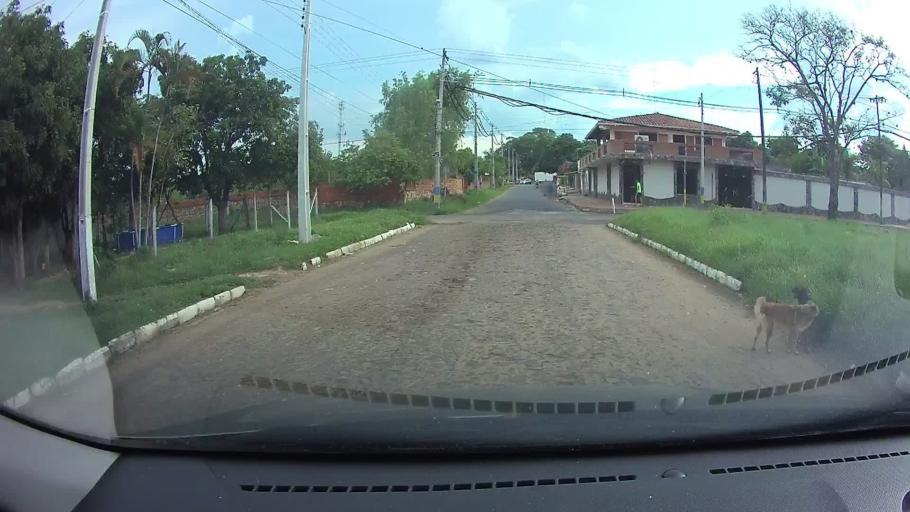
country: PY
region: Central
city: San Lorenzo
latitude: -25.2683
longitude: -57.4774
